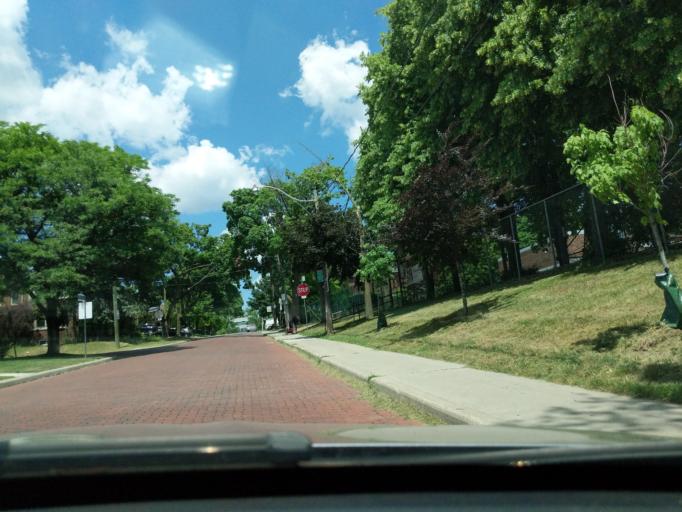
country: CA
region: Ontario
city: Toronto
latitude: 43.7020
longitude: -79.4101
